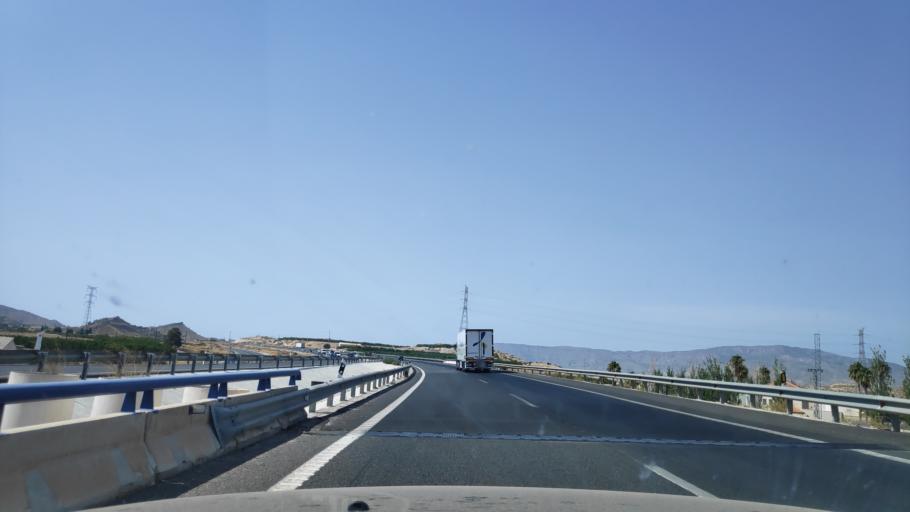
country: ES
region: Murcia
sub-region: Murcia
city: Archena
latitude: 38.1427
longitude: -1.2739
